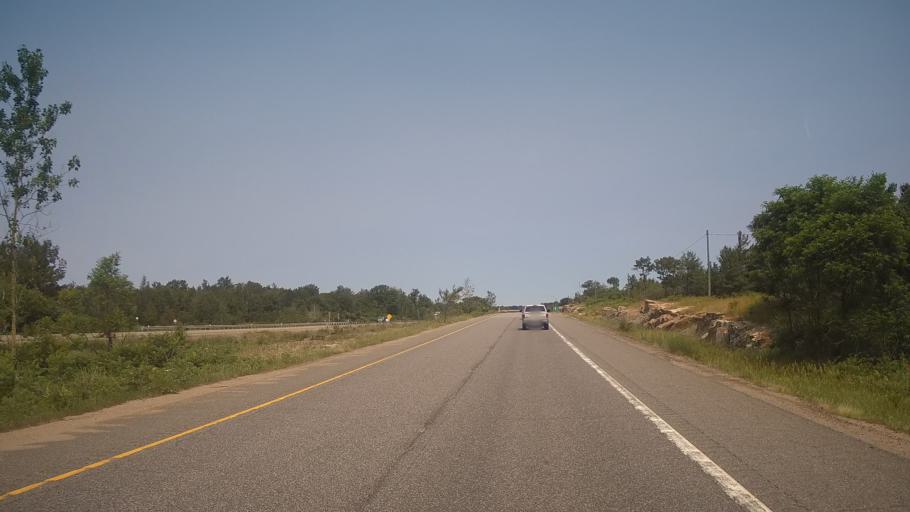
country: CA
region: Ontario
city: Midland
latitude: 44.8514
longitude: -79.7373
